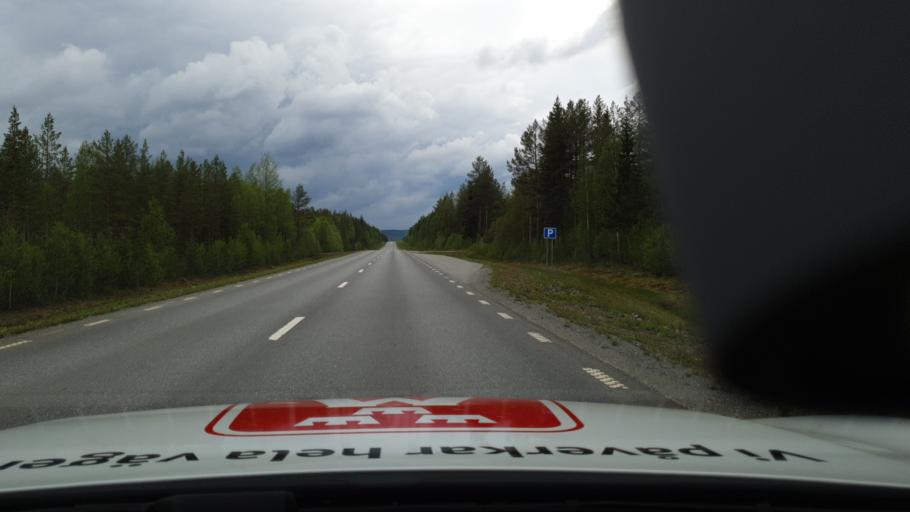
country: SE
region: Vaesterbotten
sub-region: Dorotea Kommun
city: Dorotea
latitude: 64.2636
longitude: 16.4917
